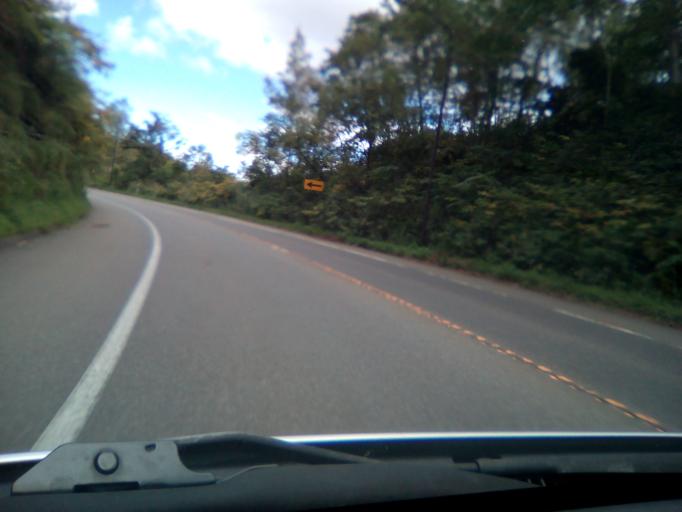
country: JP
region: Hokkaido
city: Date
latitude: 42.6088
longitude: 140.7766
